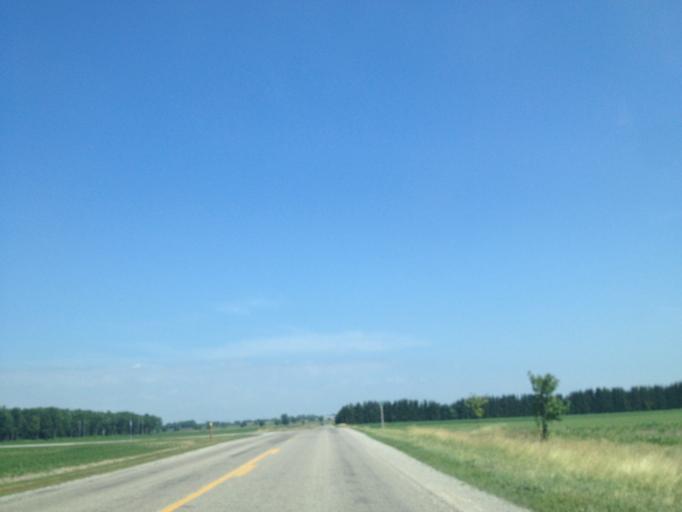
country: CA
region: Ontario
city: London
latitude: 43.1893
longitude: -81.2379
